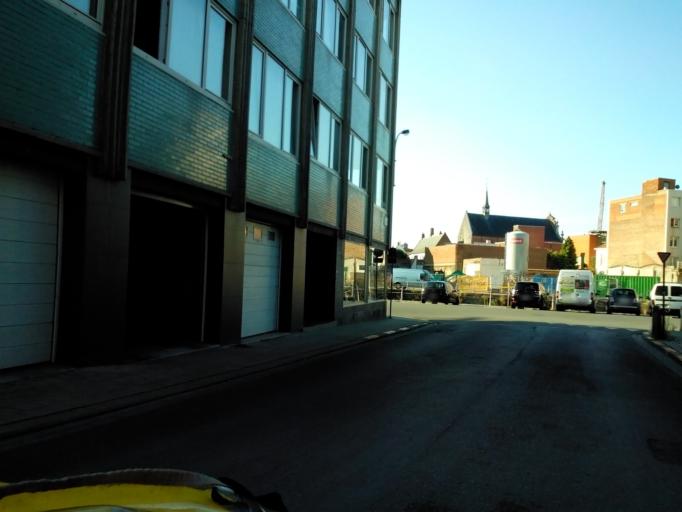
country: BE
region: Flanders
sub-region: Provincie West-Vlaanderen
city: Kortrijk
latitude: 50.8292
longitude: 3.2631
